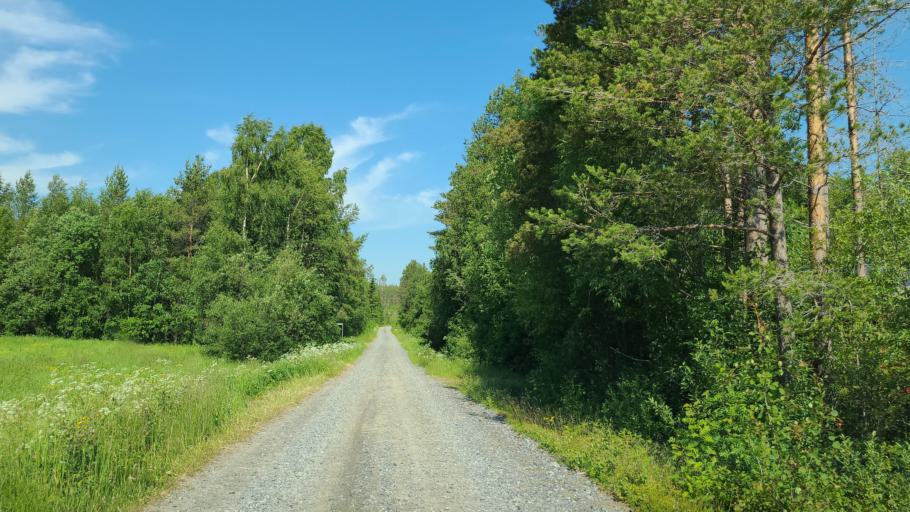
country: SE
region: Vaesterbotten
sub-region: Robertsfors Kommun
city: Robertsfors
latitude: 64.0897
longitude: 20.8377
